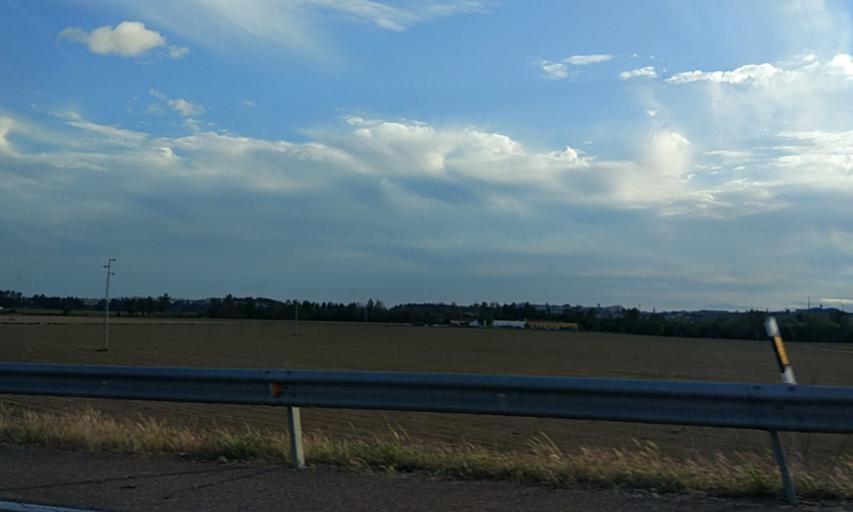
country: ES
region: Extremadura
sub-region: Provincia de Badajoz
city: Badajoz
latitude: 38.9143
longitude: -6.9505
